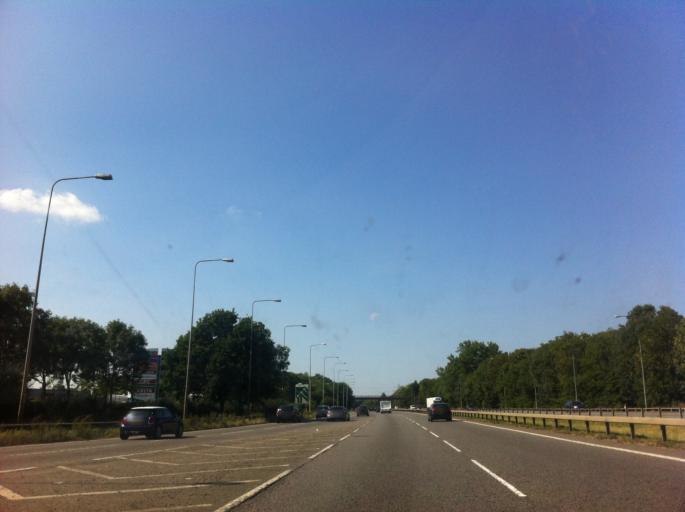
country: GB
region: England
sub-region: Northamptonshire
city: Northampton
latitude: 52.2434
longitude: -0.8396
